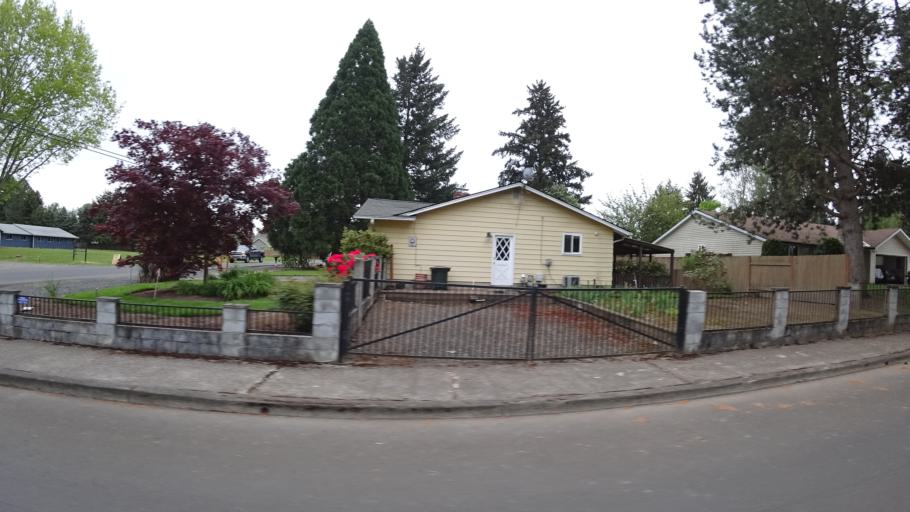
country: US
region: Oregon
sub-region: Washington County
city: Hillsboro
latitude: 45.5075
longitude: -122.9295
